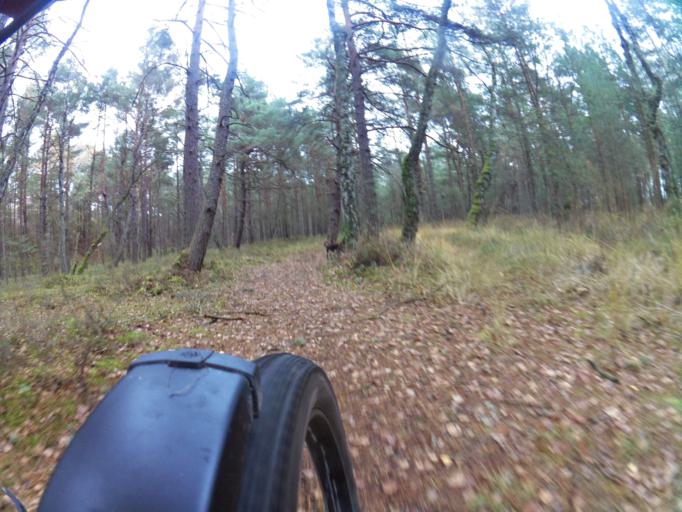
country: PL
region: Pomeranian Voivodeship
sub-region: Powiat leborski
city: Leba
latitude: 54.7728
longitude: 17.6409
